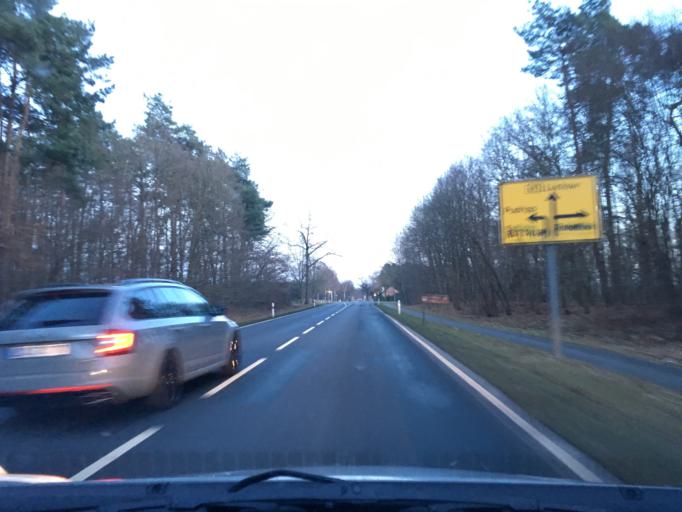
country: DE
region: Lower Saxony
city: Kusten
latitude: 52.9809
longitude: 11.1006
